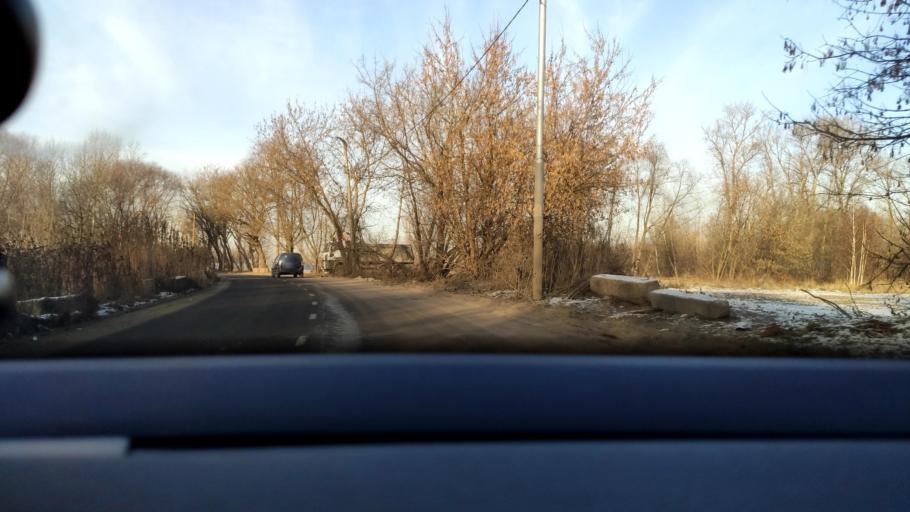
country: RU
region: Moskovskaya
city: Fili
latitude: 55.7515
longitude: 37.4585
